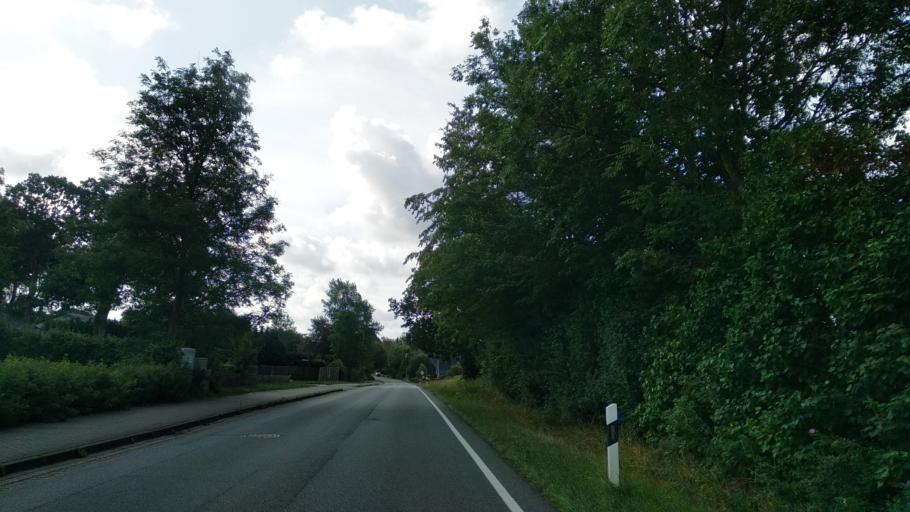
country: DE
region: Schleswig-Holstein
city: Selk
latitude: 54.4737
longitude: 9.5661
